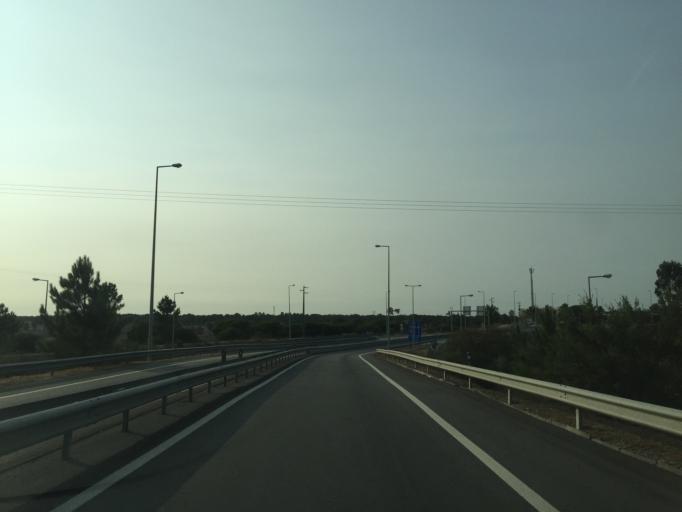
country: PT
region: Setubal
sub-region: Setubal
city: Setubal
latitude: 38.5949
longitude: -8.6722
